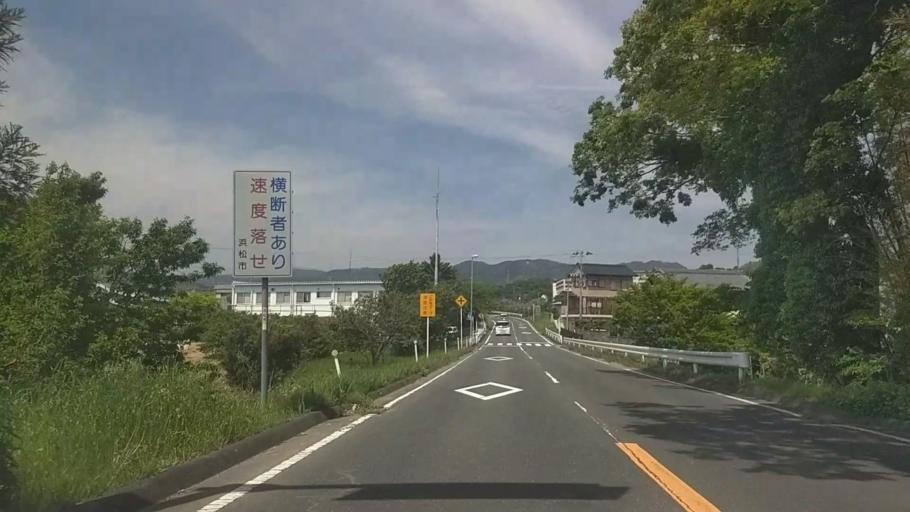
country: JP
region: Shizuoka
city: Kosai-shi
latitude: 34.7887
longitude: 137.5824
